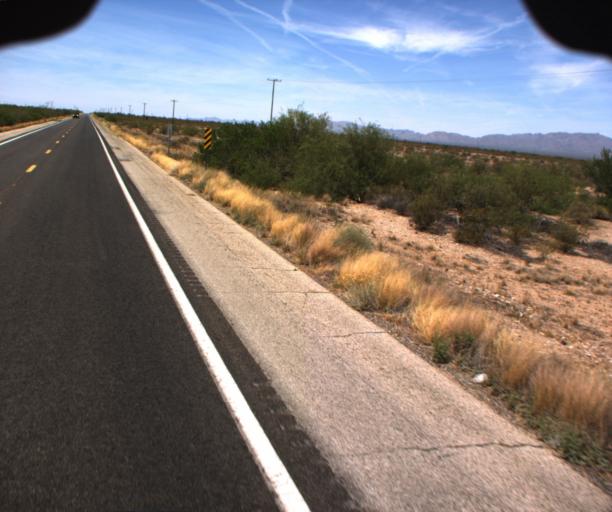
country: US
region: Arizona
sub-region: La Paz County
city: Salome
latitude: 33.9144
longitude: -113.2653
